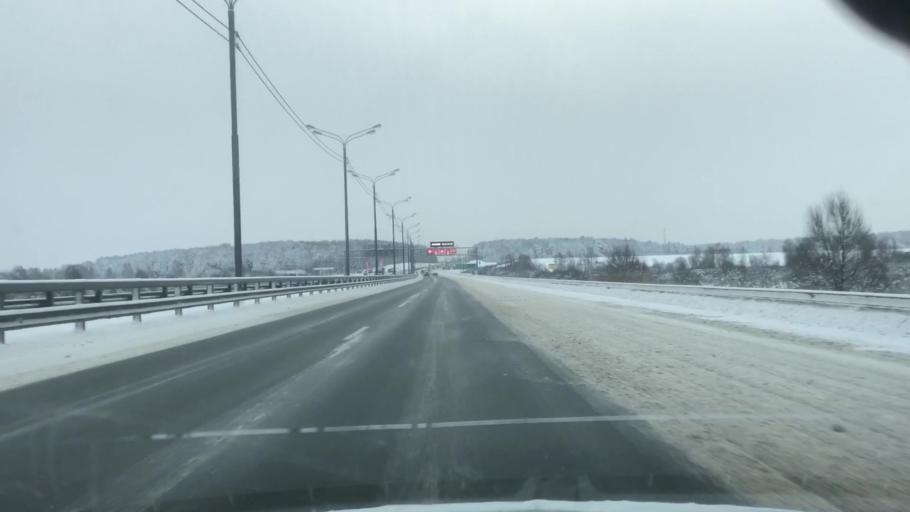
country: RU
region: Moskovskaya
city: Mikhnevo
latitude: 55.1868
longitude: 37.8993
